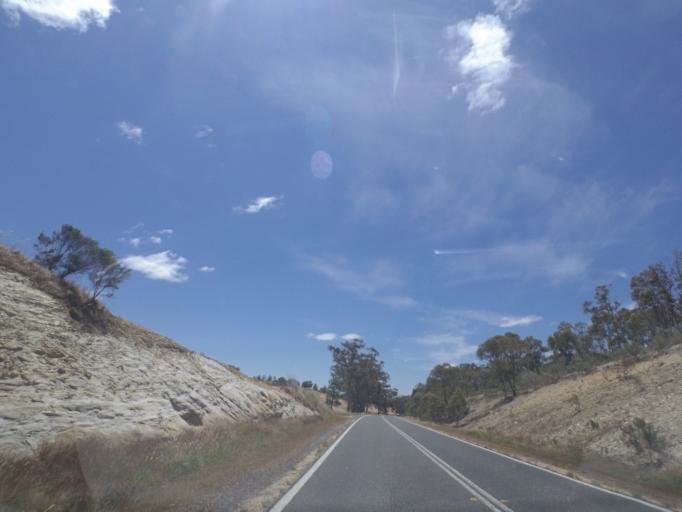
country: AU
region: Victoria
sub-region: Mount Alexander
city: Castlemaine
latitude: -37.2066
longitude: 144.1409
